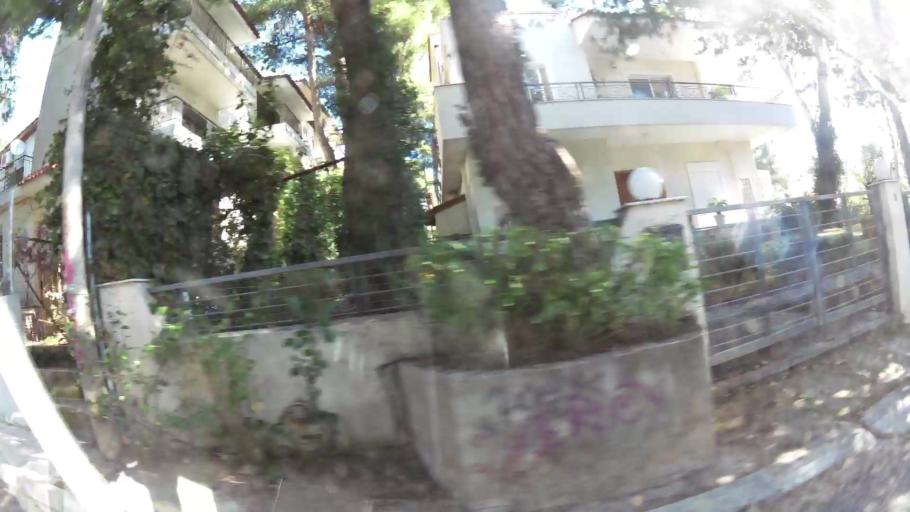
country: GR
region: Attica
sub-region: Nomarchia Anatolikis Attikis
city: Drosia
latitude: 38.1180
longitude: 23.8654
